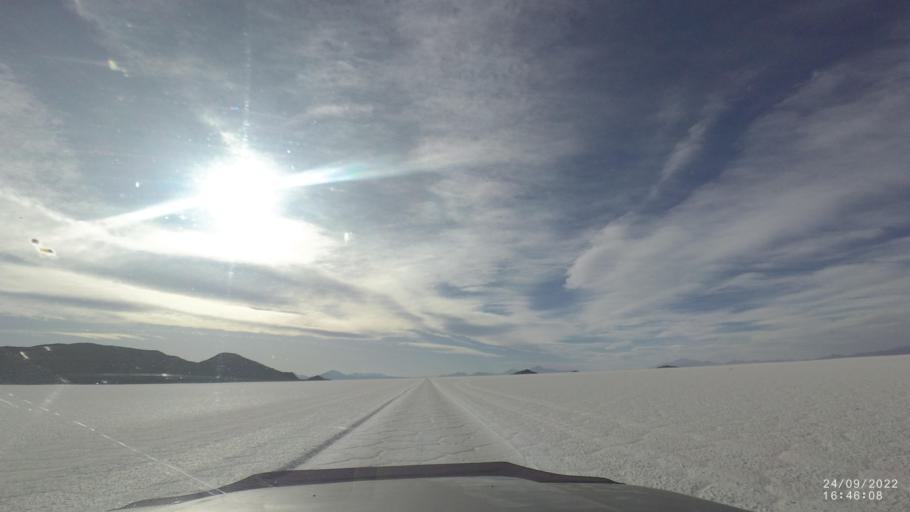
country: BO
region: Potosi
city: Colchani
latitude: -20.1407
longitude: -67.7857
